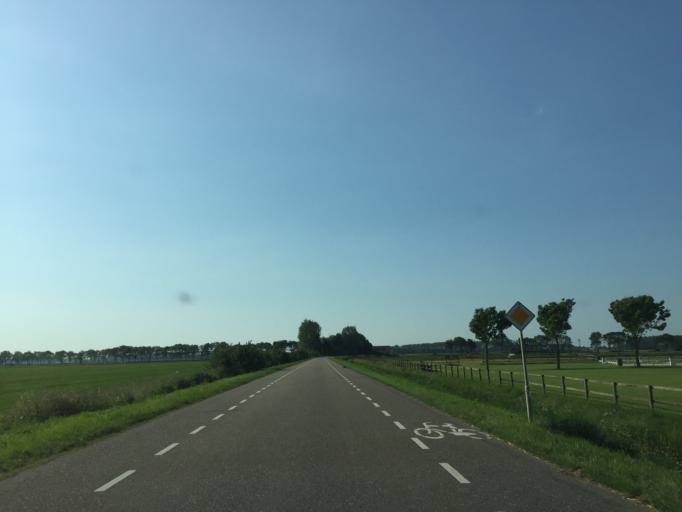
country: NL
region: Gelderland
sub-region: Gemeente Tiel
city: Tiel
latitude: 51.8591
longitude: 5.4875
